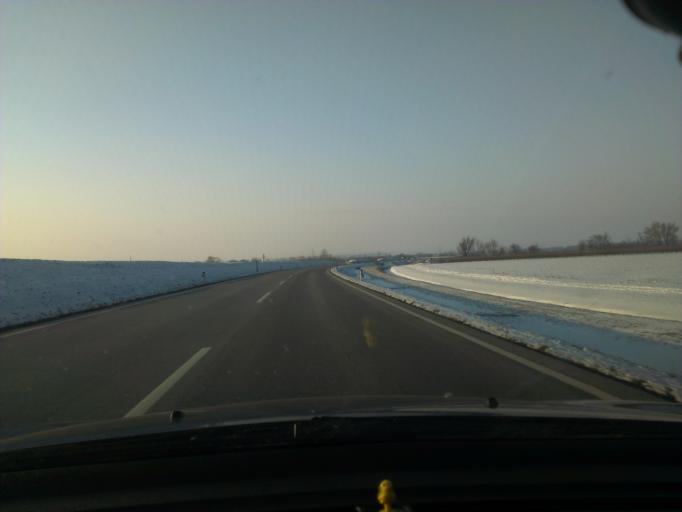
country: AT
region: Burgenland
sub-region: Eisenstadt-Umgebung
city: Schutzen am Gebirge
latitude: 47.8515
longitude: 16.6050
